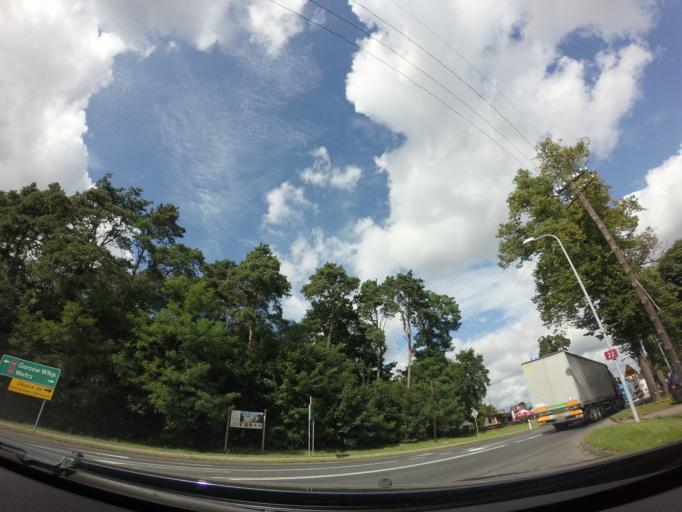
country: PL
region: Lubusz
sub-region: Powiat strzelecko-drezdenecki
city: Dobiegniew
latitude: 52.9661
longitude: 15.7495
